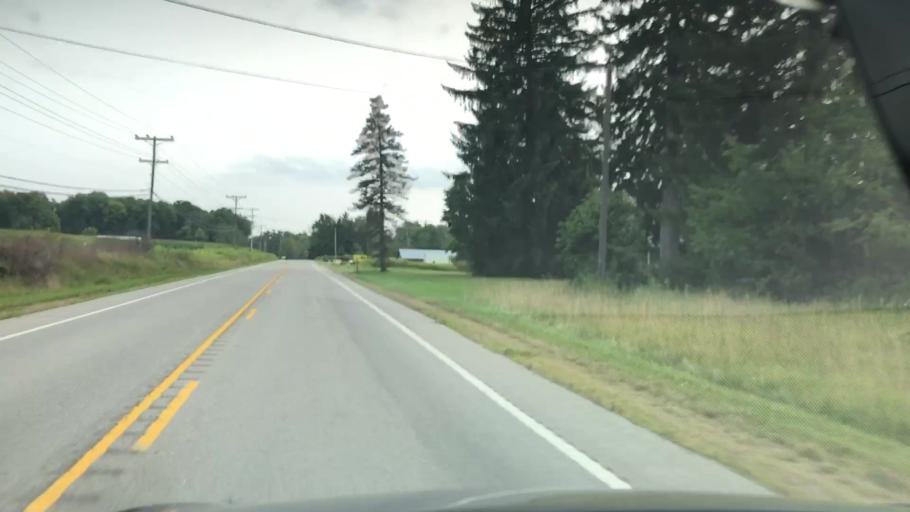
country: US
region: Pennsylvania
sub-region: Crawford County
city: Titusville
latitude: 41.5951
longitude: -79.6816
